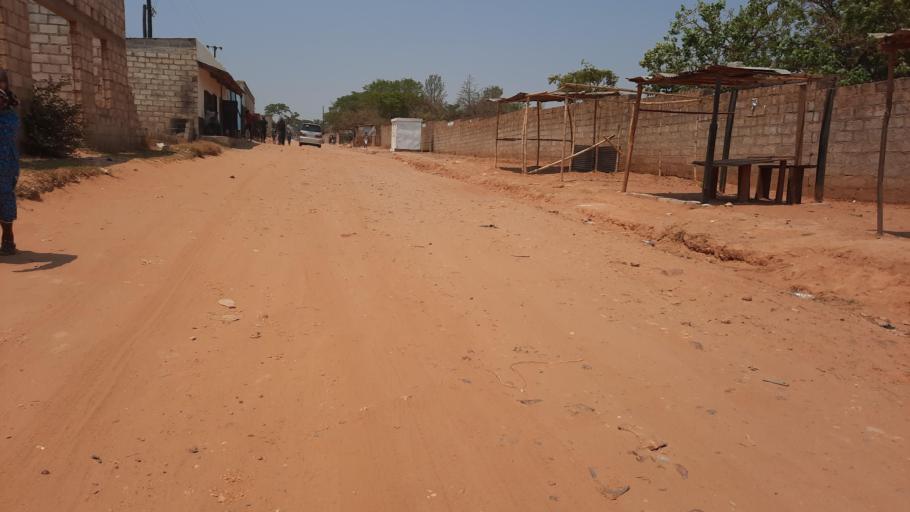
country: ZM
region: Lusaka
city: Lusaka
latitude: -15.4089
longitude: 28.3798
